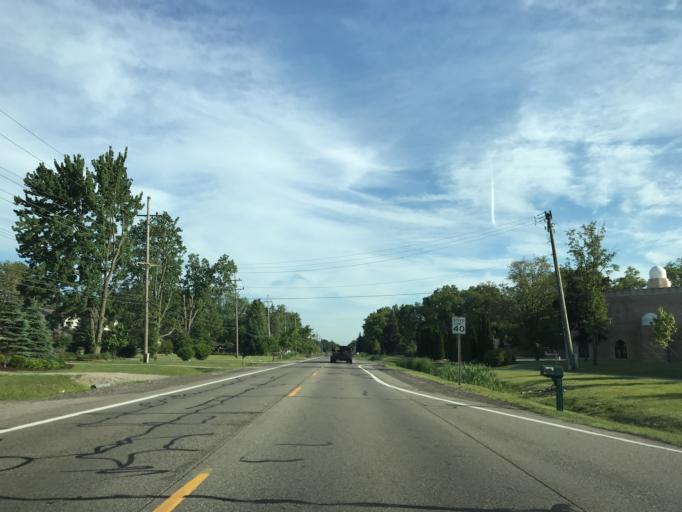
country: US
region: Michigan
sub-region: Oakland County
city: Farmington
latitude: 42.4470
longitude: -83.3561
